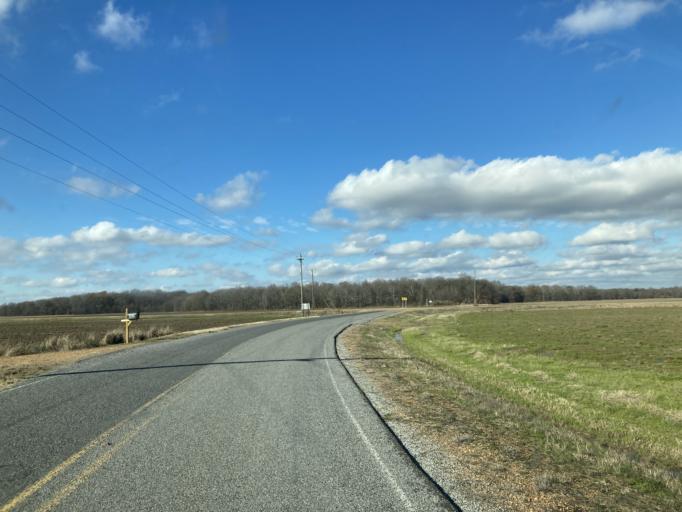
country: US
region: Mississippi
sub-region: Yazoo County
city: Yazoo City
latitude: 32.9610
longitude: -90.4885
